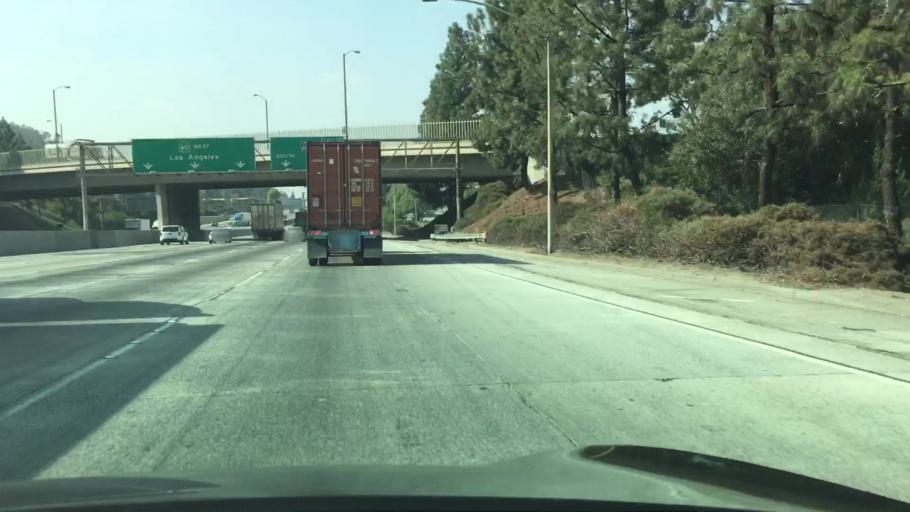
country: US
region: California
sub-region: Los Angeles County
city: Avocado Heights
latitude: 34.0267
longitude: -118.0078
